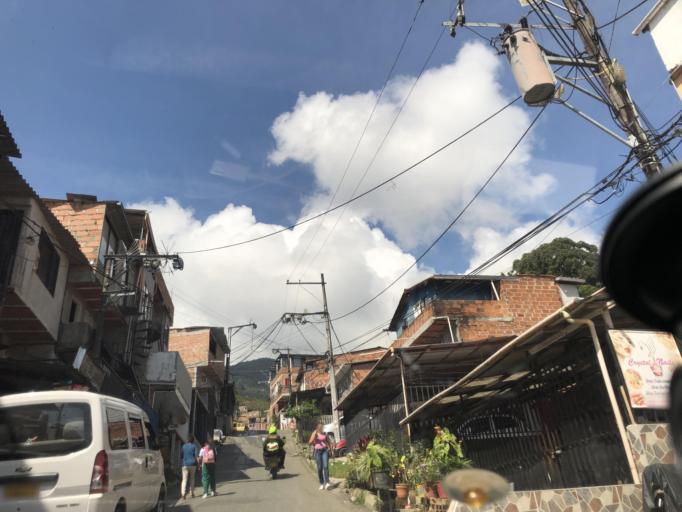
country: CO
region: Antioquia
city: Bello
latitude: 6.3156
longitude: -75.5852
